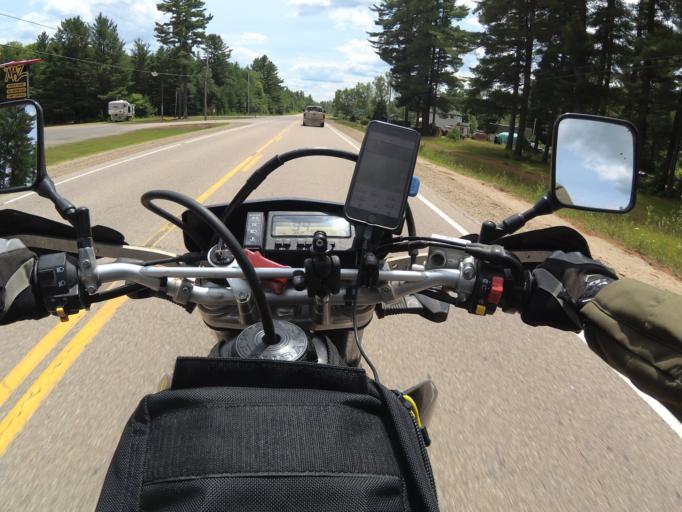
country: CA
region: Ontario
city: Greater Napanee
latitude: 44.8475
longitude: -77.1780
